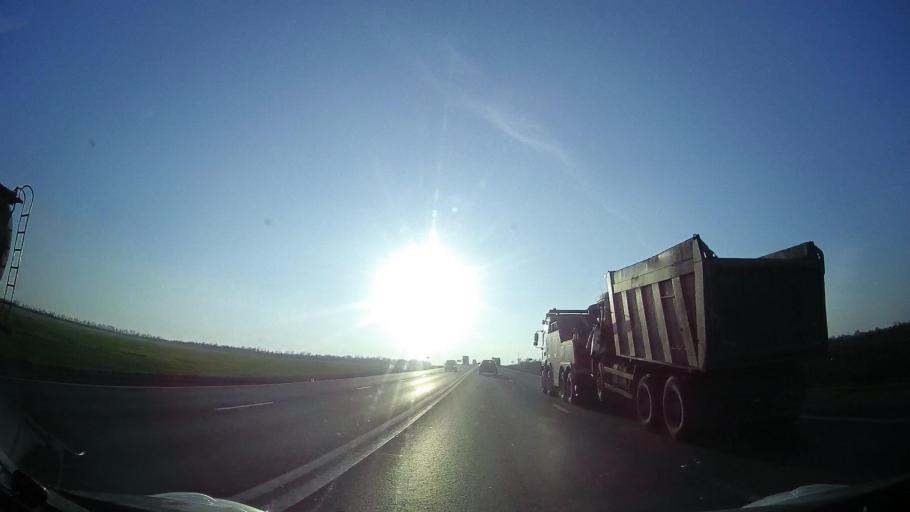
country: RU
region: Rostov
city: Bataysk
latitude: 47.0926
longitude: 39.7998
